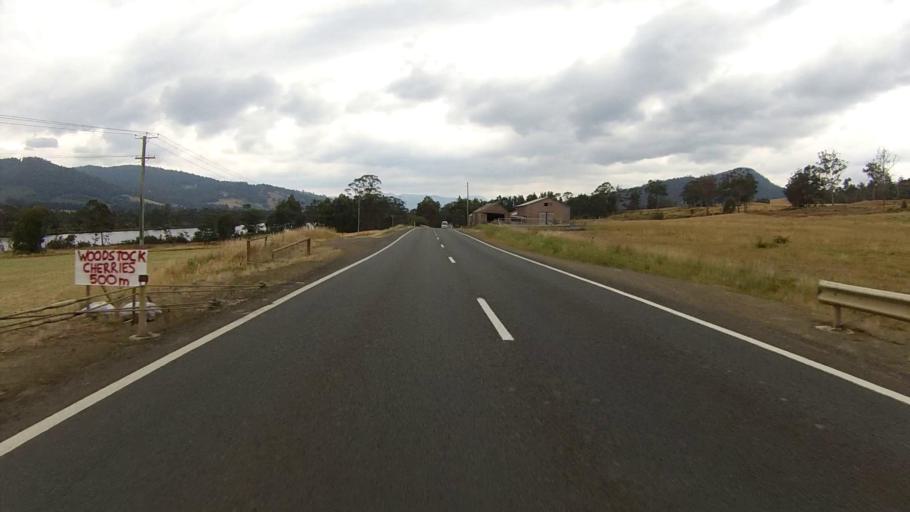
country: AU
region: Tasmania
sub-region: Huon Valley
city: Franklin
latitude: -43.0840
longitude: 147.0303
